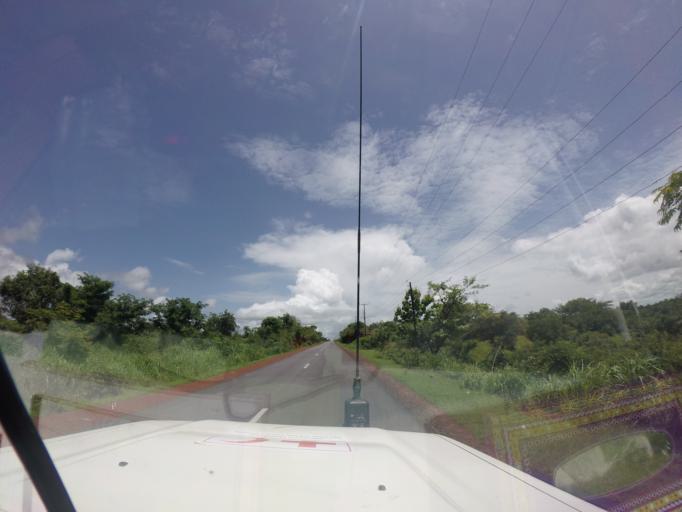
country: GN
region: Faranah
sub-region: Faranah Prefecture
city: Faranah
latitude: 10.0378
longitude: -10.7650
